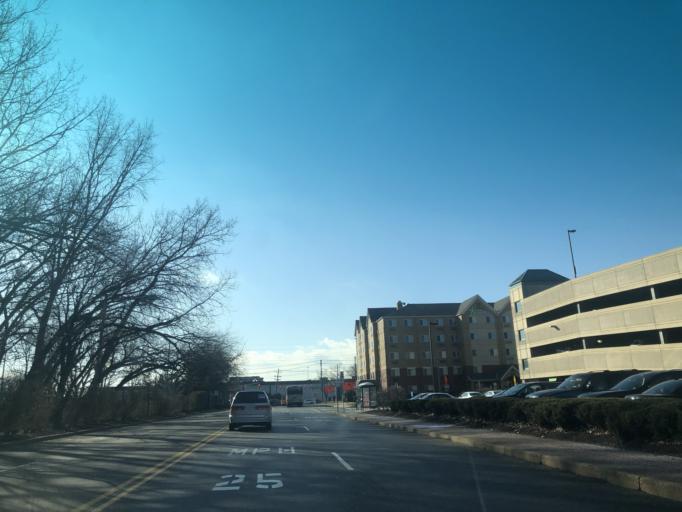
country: US
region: New Jersey
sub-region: Hudson County
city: Secaucus
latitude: 40.7840
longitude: -74.0436
